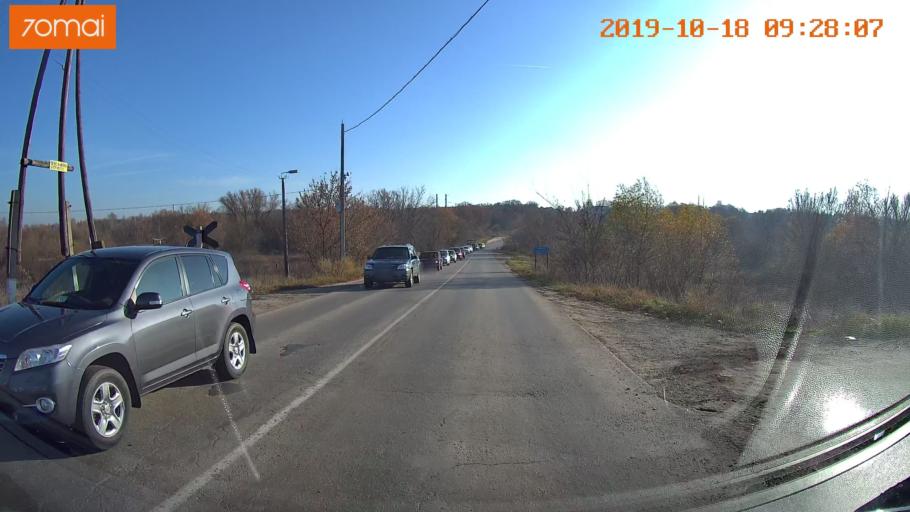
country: RU
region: Tula
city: Yefremov
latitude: 53.1341
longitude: 38.1328
